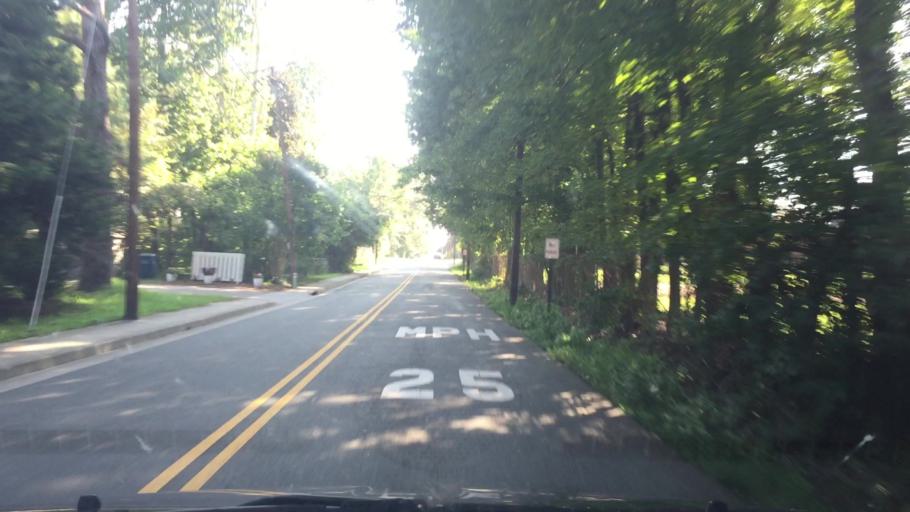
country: US
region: Virginia
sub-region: Hanover County
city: Ashland
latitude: 37.7560
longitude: -77.4893
